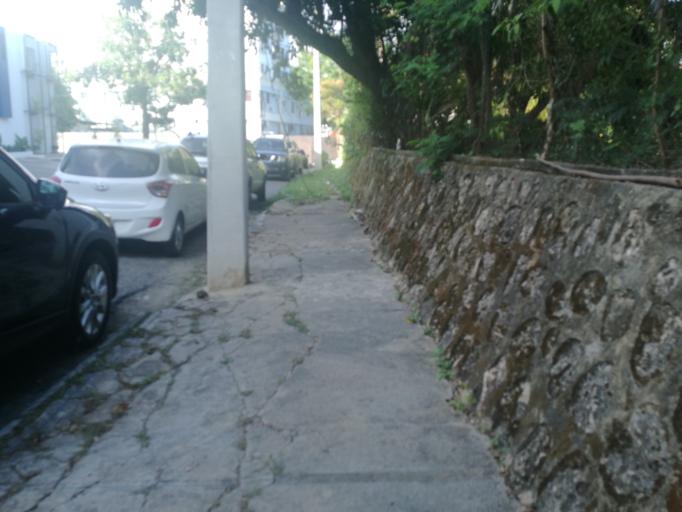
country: DO
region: Nacional
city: La Julia
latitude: 18.4763
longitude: -69.9452
